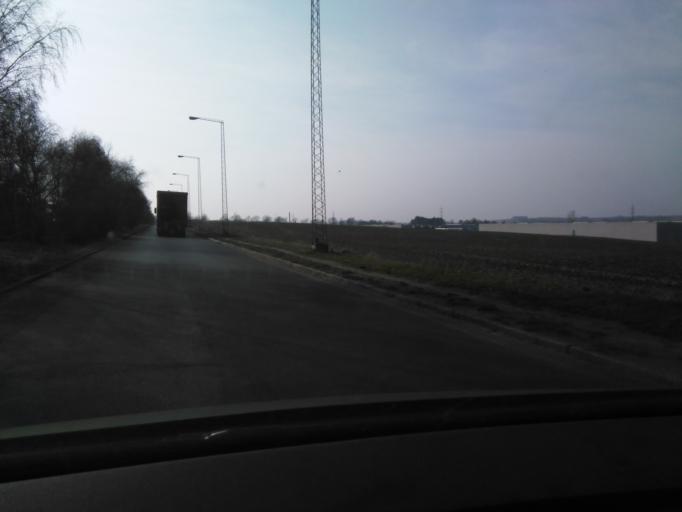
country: DK
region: Central Jutland
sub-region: Arhus Kommune
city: Arhus
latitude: 56.2065
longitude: 10.1872
